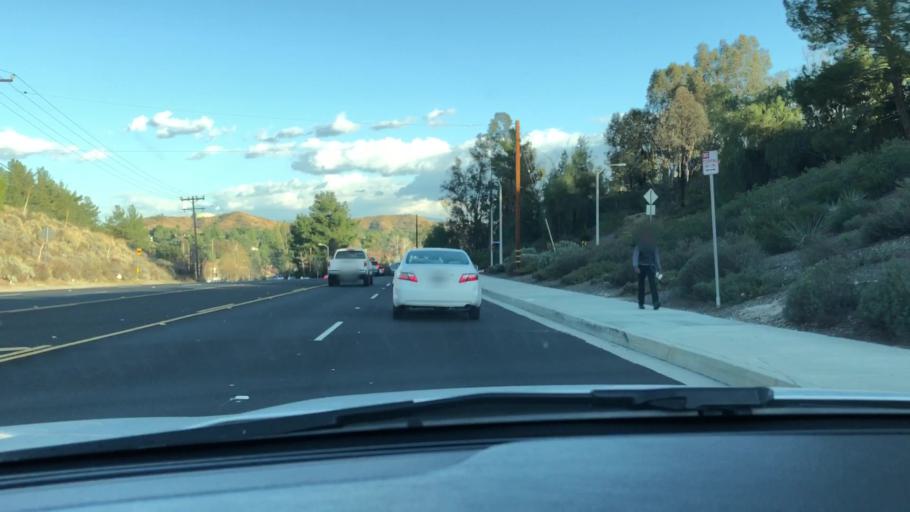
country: US
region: California
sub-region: Los Angeles County
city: Santa Clarita
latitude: 34.4607
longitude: -118.5405
